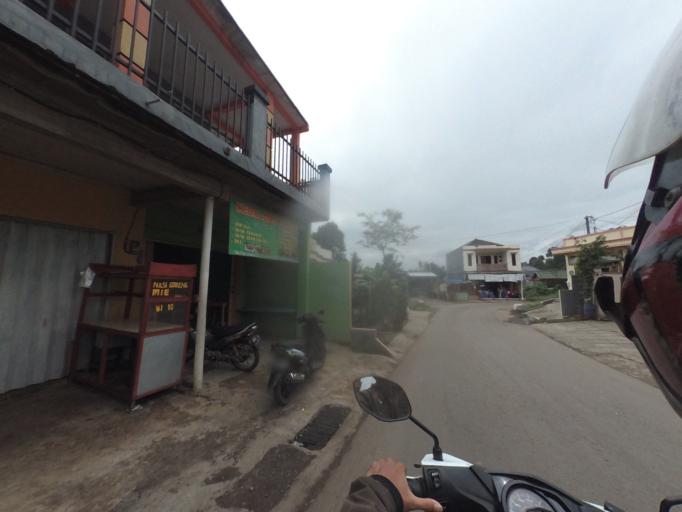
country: ID
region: West Java
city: Bogor
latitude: -6.6378
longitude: 106.7501
